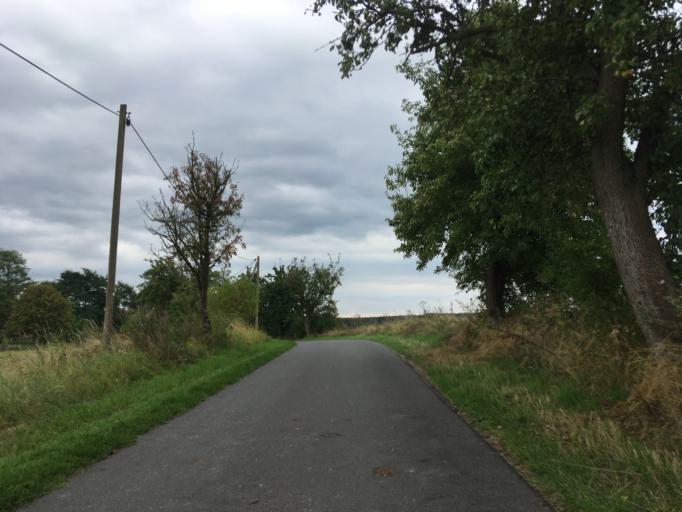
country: DE
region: Brandenburg
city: Friedrichswalde
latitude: 53.0250
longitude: 13.7244
